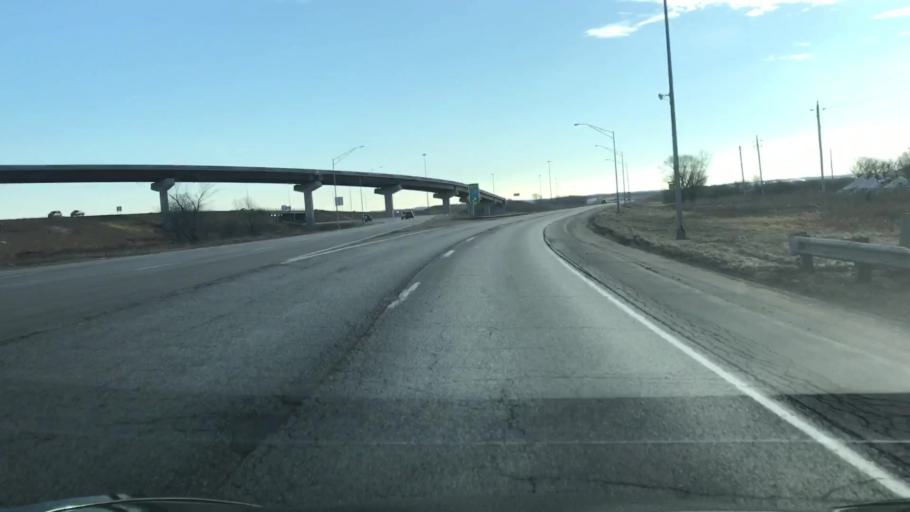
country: US
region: Iowa
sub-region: Pottawattamie County
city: Council Bluffs
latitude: 41.2308
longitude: -95.8437
